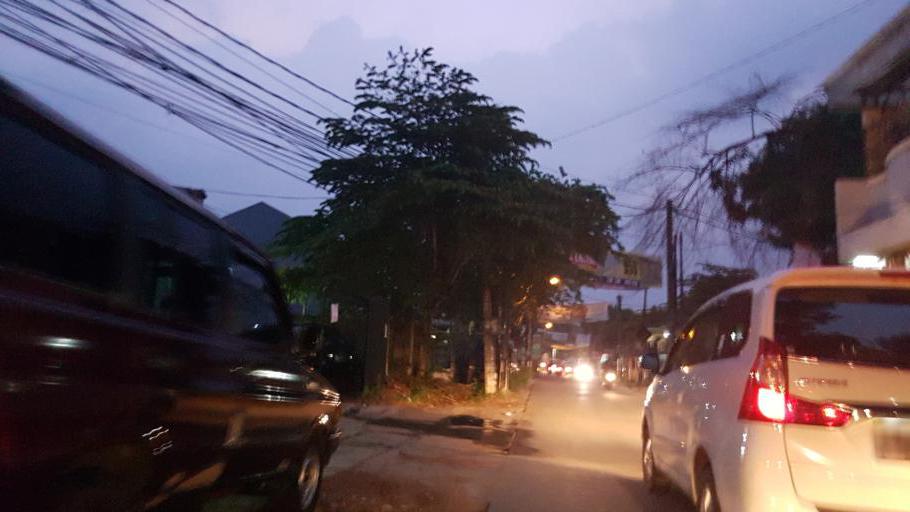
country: ID
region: West Java
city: Pamulang
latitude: -6.3410
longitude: 106.7974
